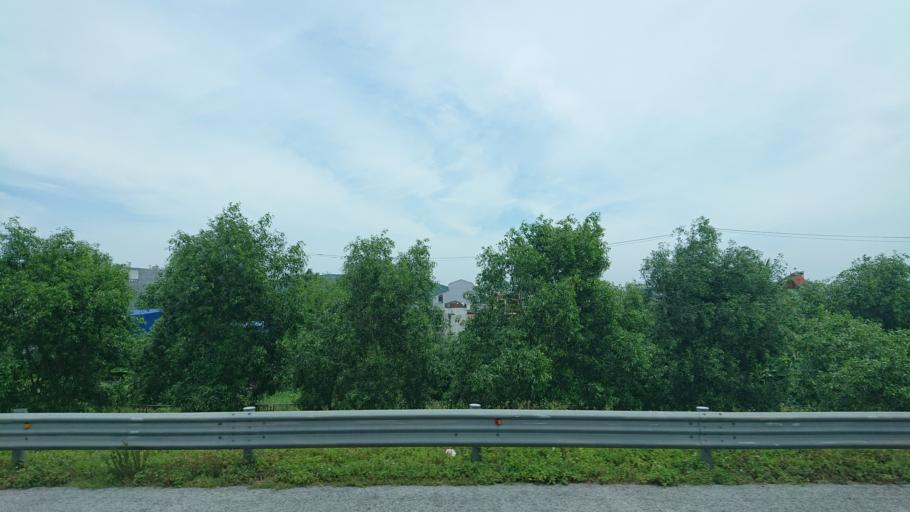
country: VN
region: Hai Phong
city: Nui Doi
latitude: 20.7707
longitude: 106.6177
